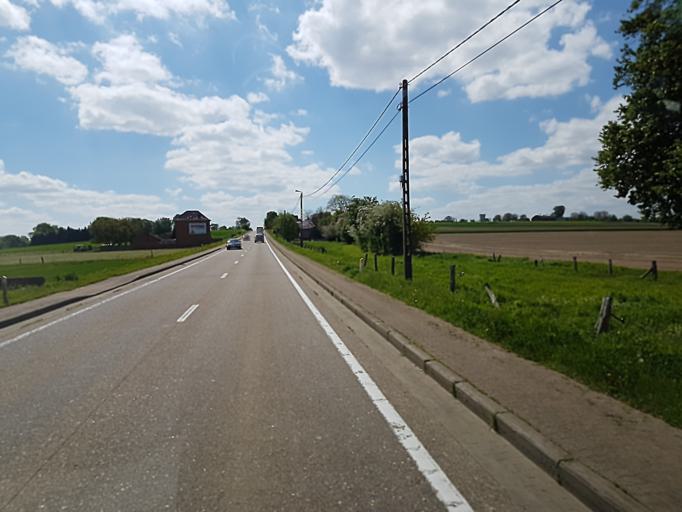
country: BE
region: Flanders
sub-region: Provincie Vlaams-Brabant
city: Bekkevoort
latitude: 50.9481
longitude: 4.9959
